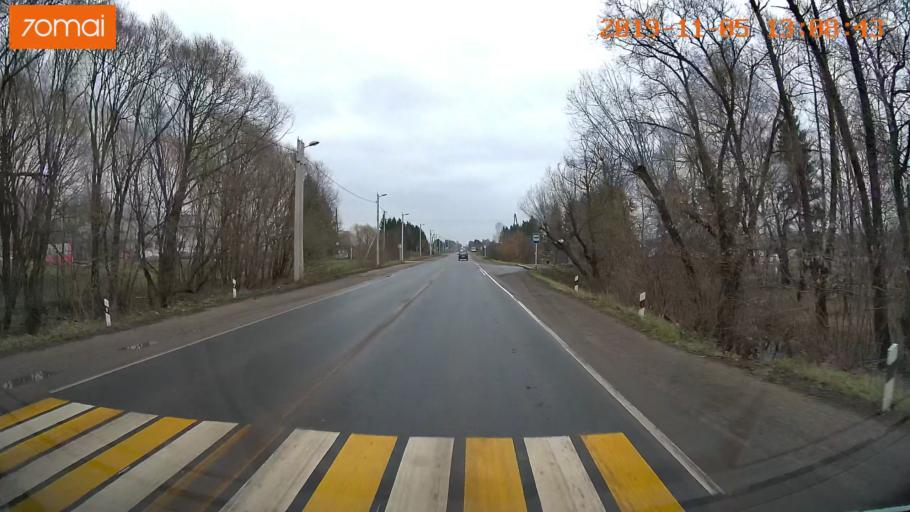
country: RU
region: Ivanovo
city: Kitovo
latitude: 56.8642
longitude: 41.2929
